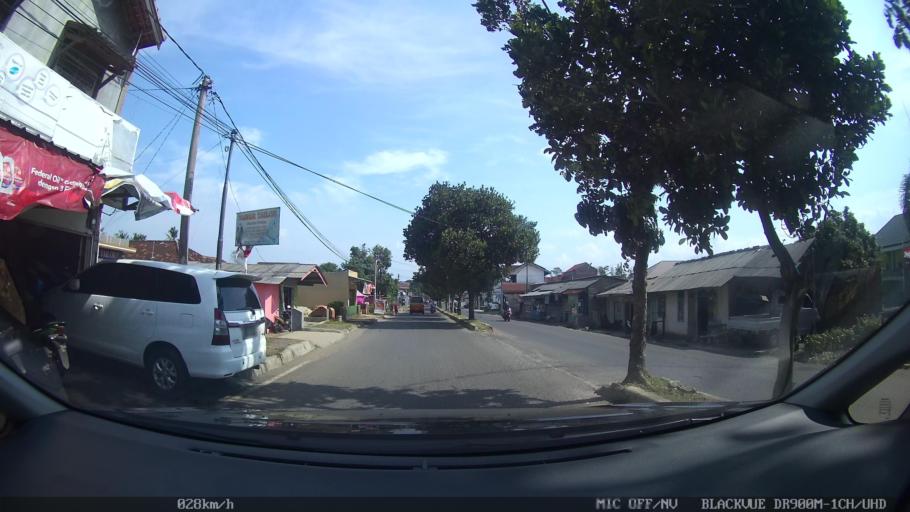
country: ID
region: Lampung
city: Kedaton
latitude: -5.3628
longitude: 105.2352
